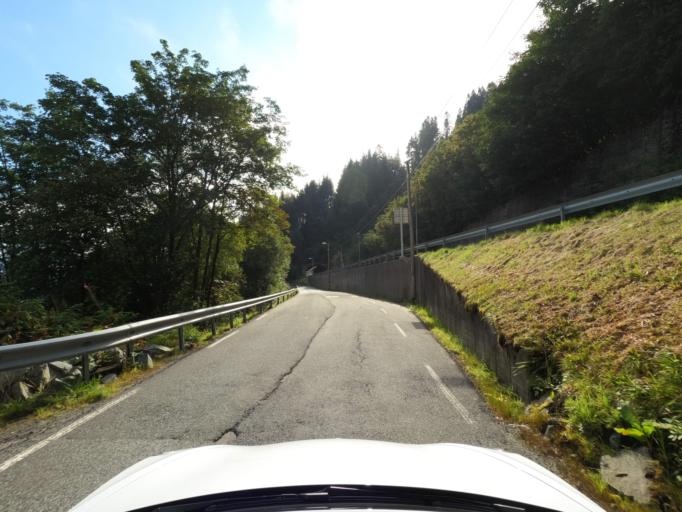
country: NO
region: Hordaland
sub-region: Bergen
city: Indre Arna
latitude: 60.4233
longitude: 5.5089
